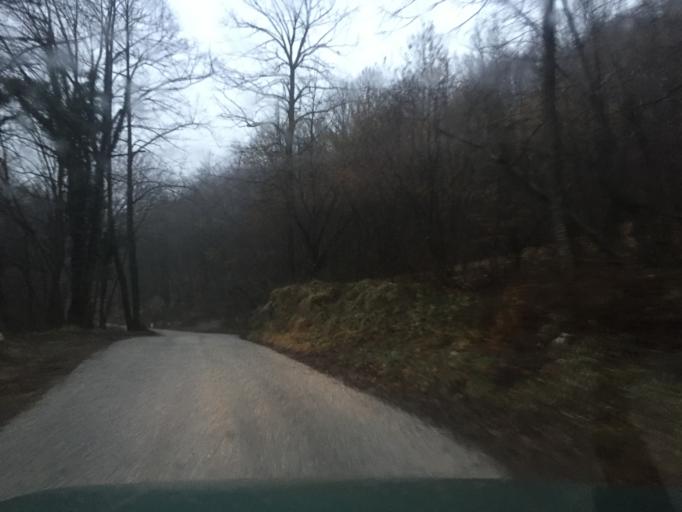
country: SI
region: Kanal
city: Kanal
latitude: 46.0519
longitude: 13.6710
